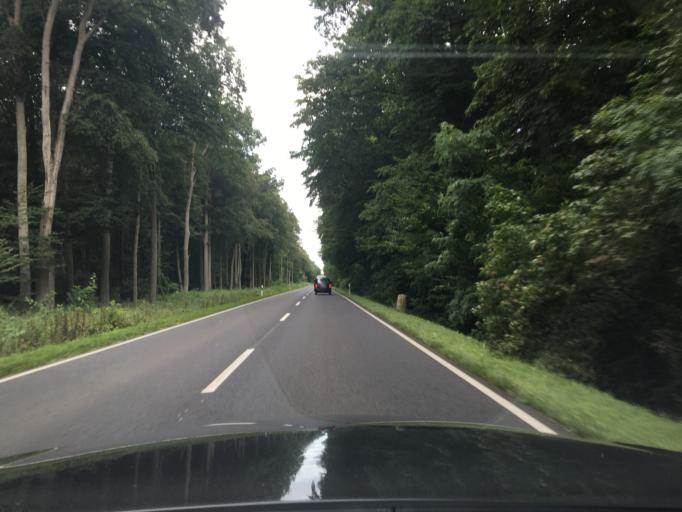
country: DE
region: Brandenburg
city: Gransee
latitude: 53.0615
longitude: 13.1874
